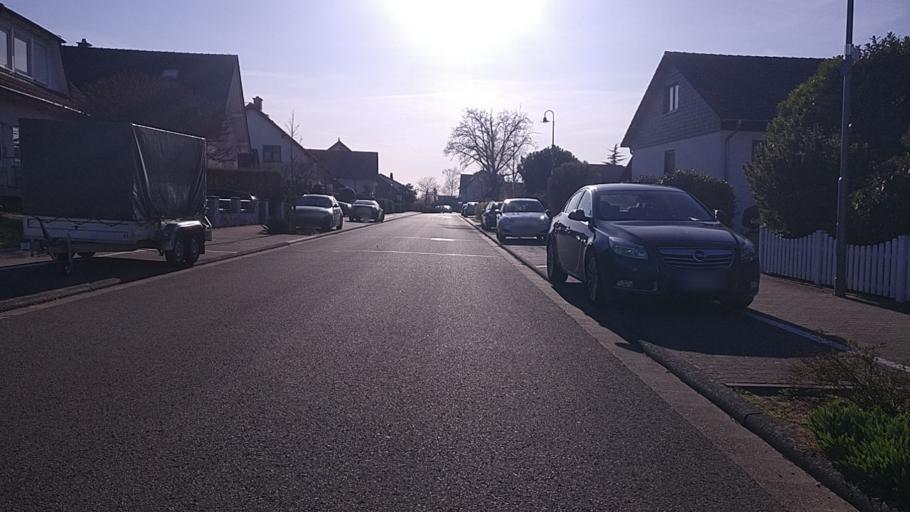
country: DE
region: Rheinland-Pfalz
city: Gau-Algesheim
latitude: 49.9697
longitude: 8.0307
